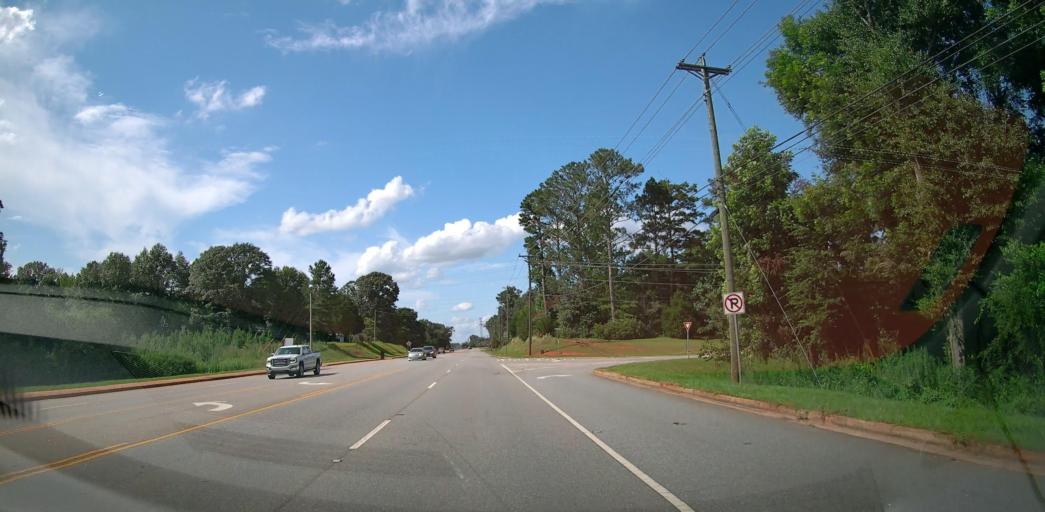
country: US
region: Georgia
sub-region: Houston County
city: Perry
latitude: 32.5389
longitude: -83.6908
